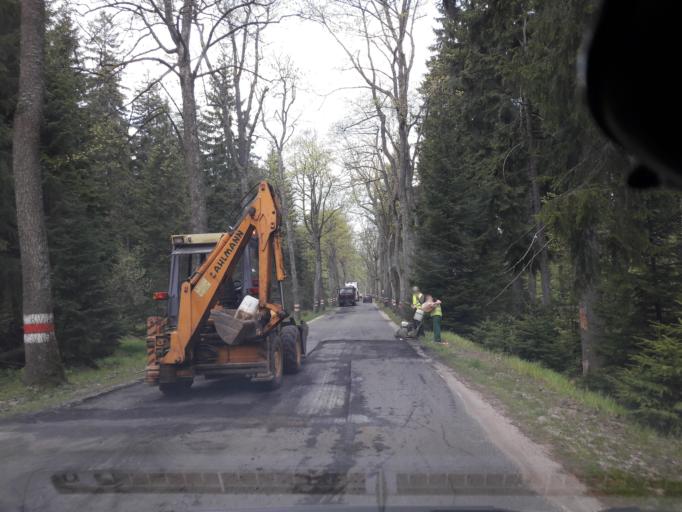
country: PL
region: Lower Silesian Voivodeship
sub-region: Powiat klodzki
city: Radkow
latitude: 50.4666
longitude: 16.3450
